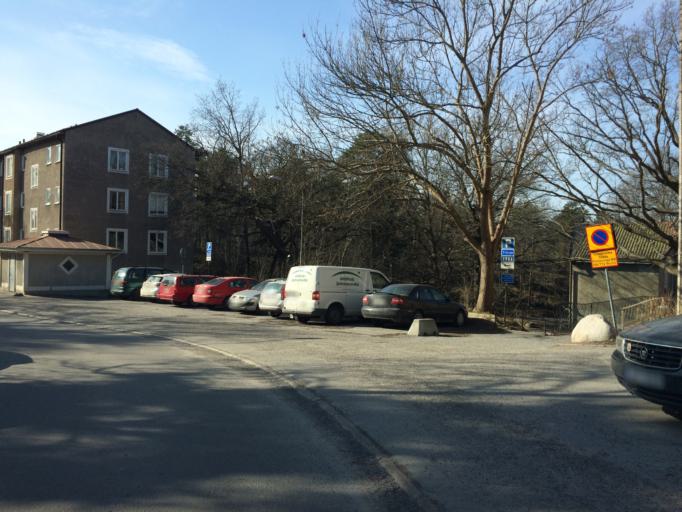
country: SE
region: Stockholm
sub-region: Stockholms Kommun
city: Arsta
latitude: 59.2905
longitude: 18.0029
